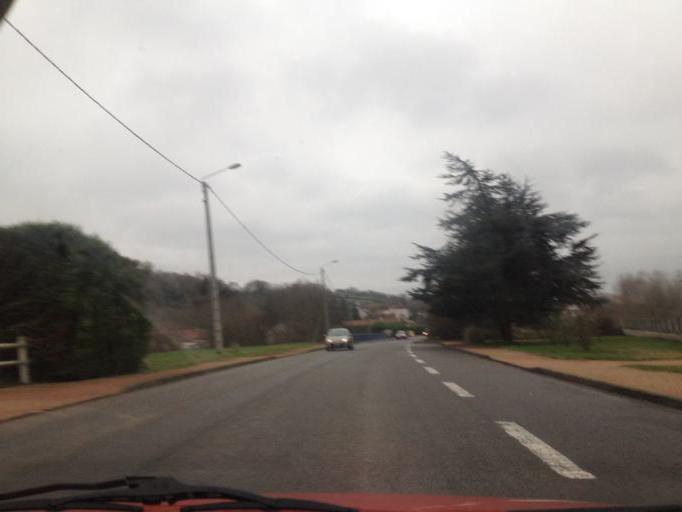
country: FR
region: Auvergne
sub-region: Departement de l'Allier
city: Saint-Germain-des-Fosses
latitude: 46.1929
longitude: 3.4314
